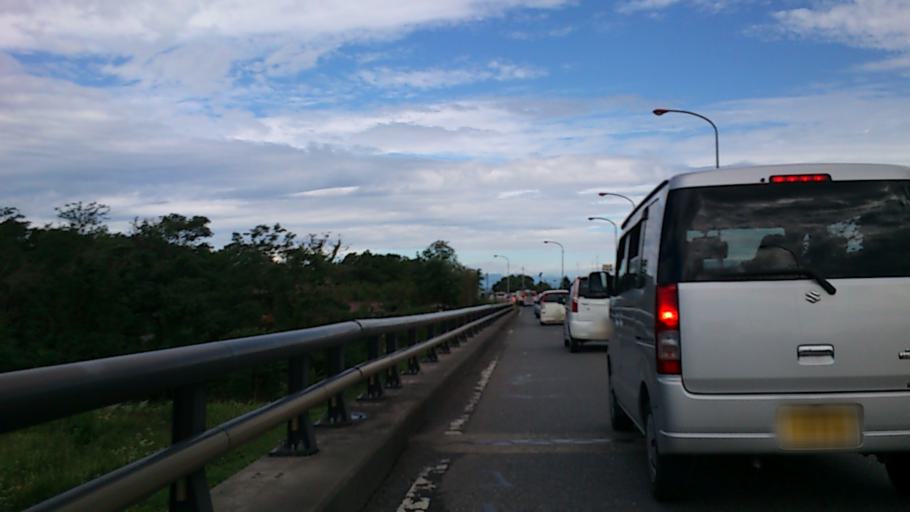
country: JP
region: Gunma
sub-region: Sawa-gun
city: Tamamura
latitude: 36.2683
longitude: 139.1198
